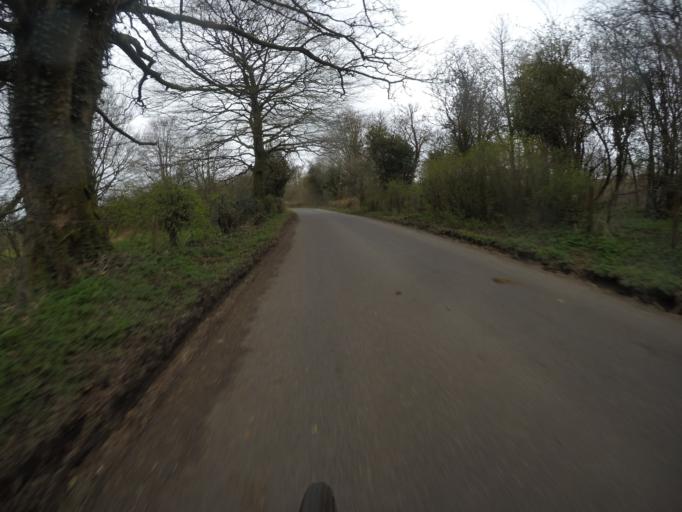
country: GB
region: Scotland
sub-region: East Ayrshire
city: Galston
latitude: 55.6081
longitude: -4.3915
